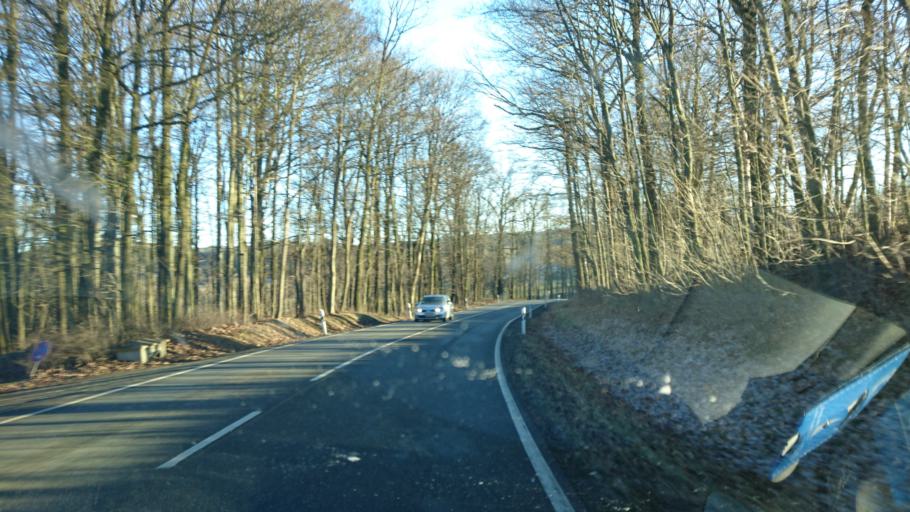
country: DE
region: Thuringia
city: Lohma
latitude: 50.5804
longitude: 11.8443
